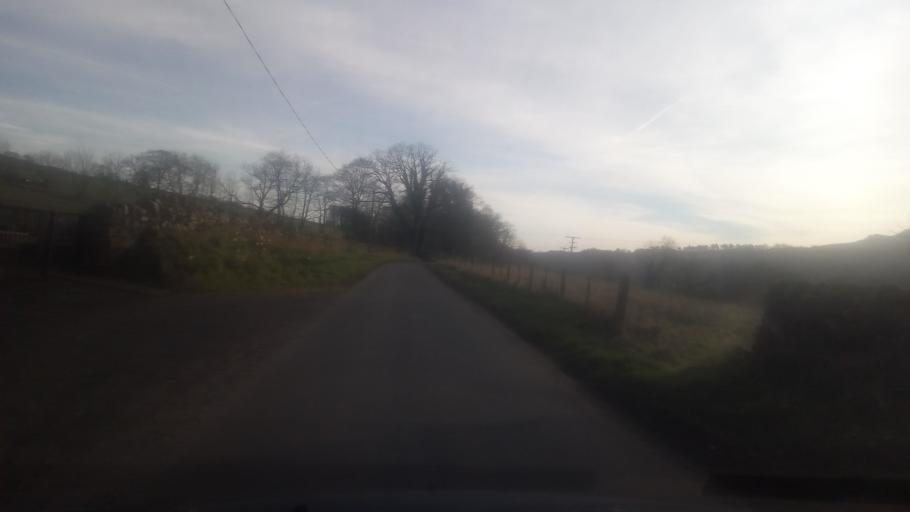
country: GB
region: Scotland
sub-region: The Scottish Borders
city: Jedburgh
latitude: 55.4538
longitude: -2.6330
